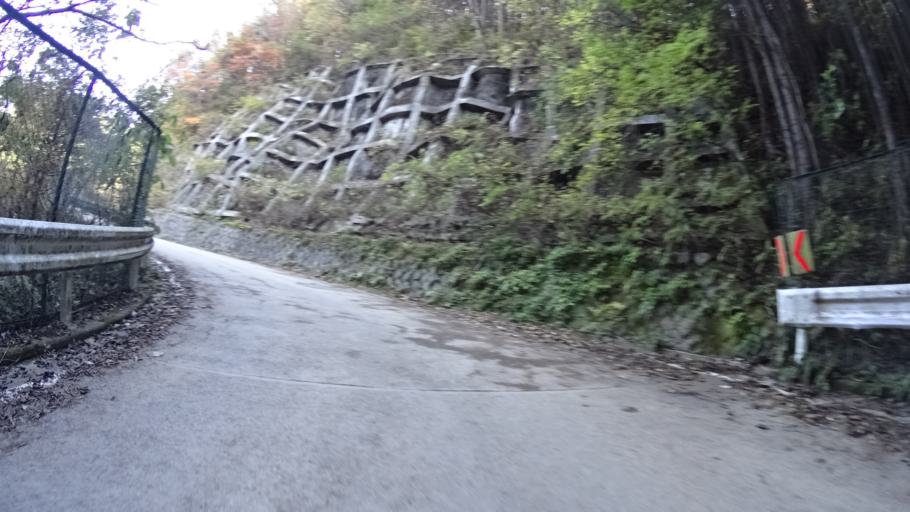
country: JP
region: Yamanashi
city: Uenohara
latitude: 35.6572
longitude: 139.1674
